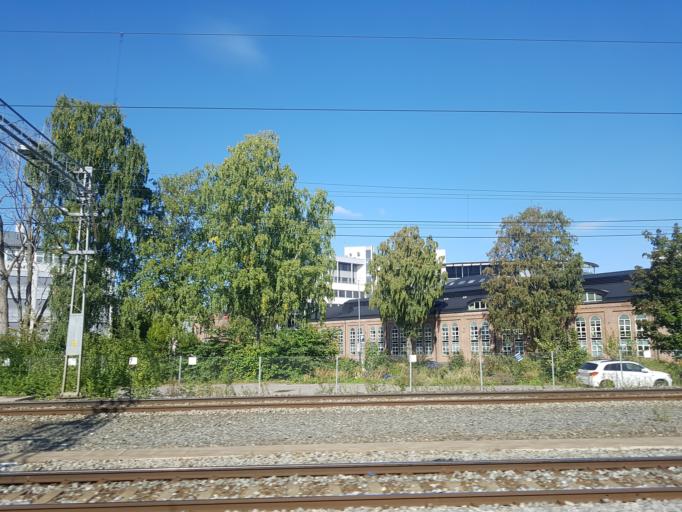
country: NO
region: Oslo
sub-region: Oslo
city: Sjolyststranda
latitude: 59.9235
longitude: 10.6755
